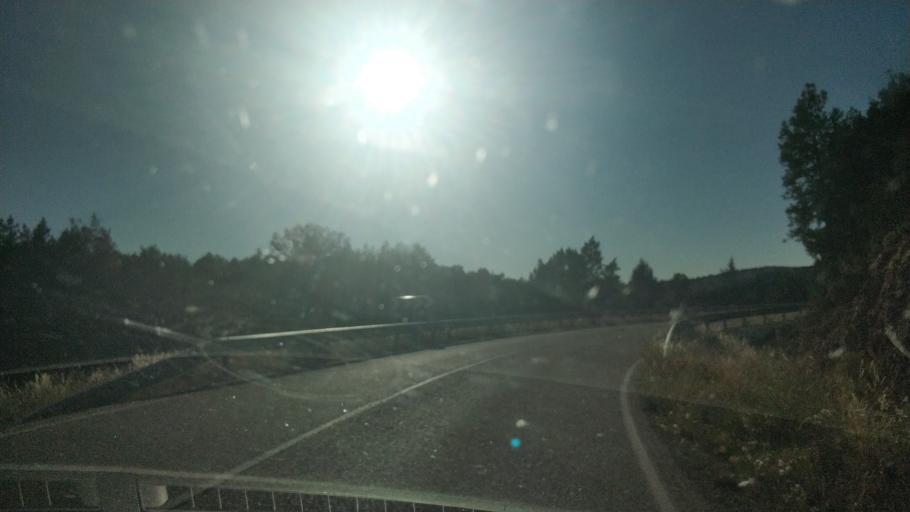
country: ES
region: Castille and Leon
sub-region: Provincia de Soria
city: Liceras
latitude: 41.4342
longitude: -3.2095
